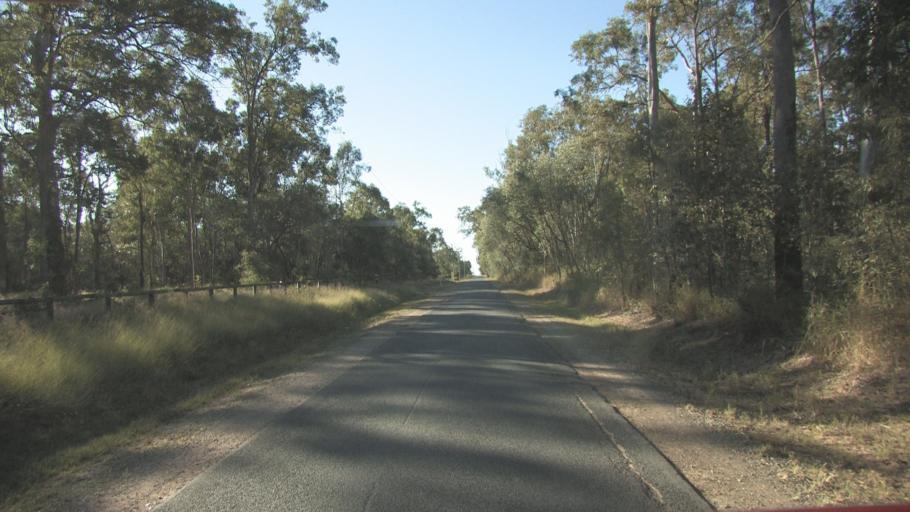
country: AU
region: Queensland
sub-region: Logan
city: North Maclean
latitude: -27.7876
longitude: 153.0386
